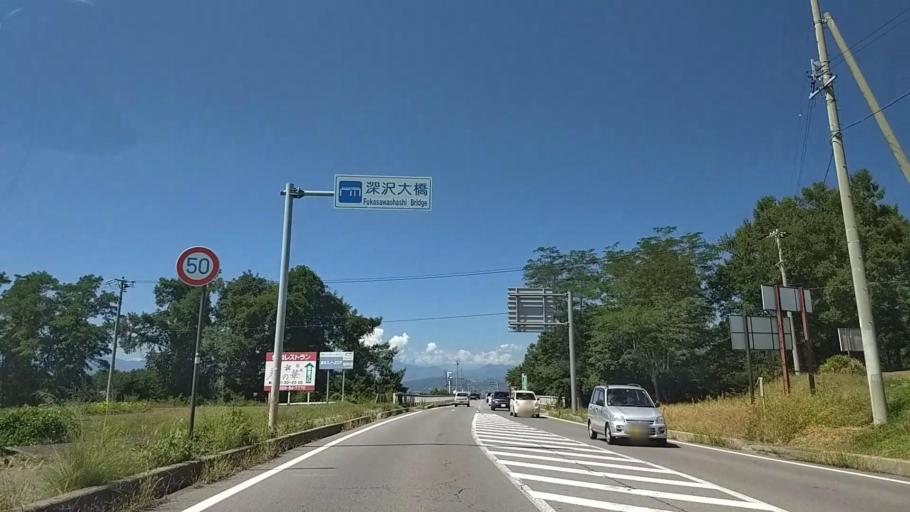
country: JP
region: Nagano
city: Komoro
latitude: 36.3513
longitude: 138.4041
